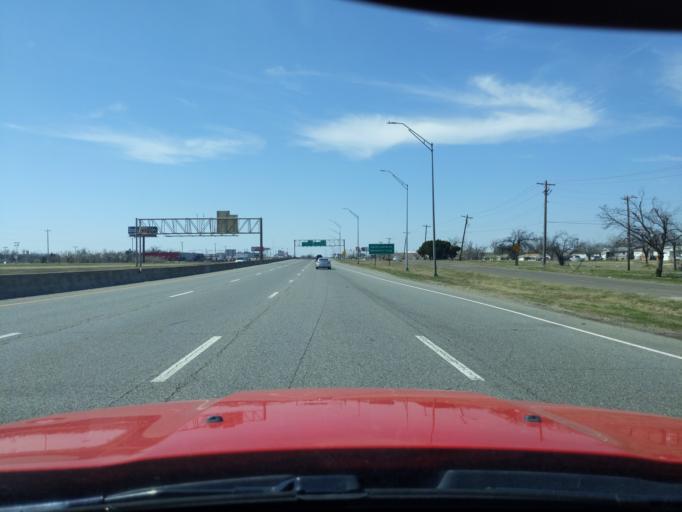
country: US
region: Oklahoma
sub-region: Cleveland County
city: Moore
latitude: 35.3921
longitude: -97.4983
